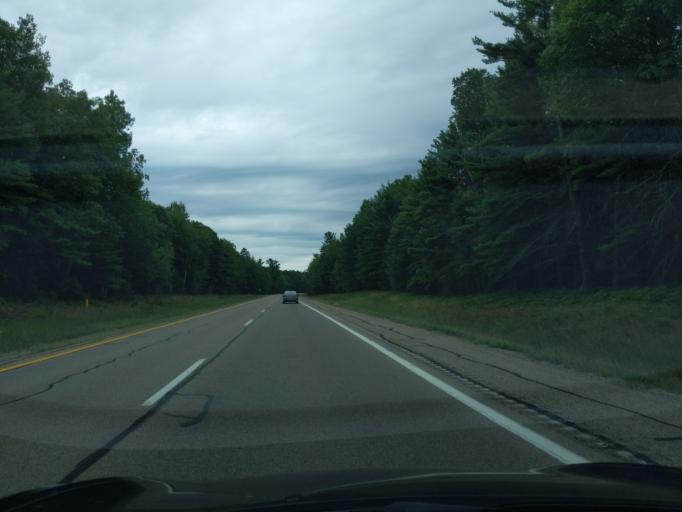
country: US
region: Michigan
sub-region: Roscommon County
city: Houghton Lake
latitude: 44.2299
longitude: -84.7998
